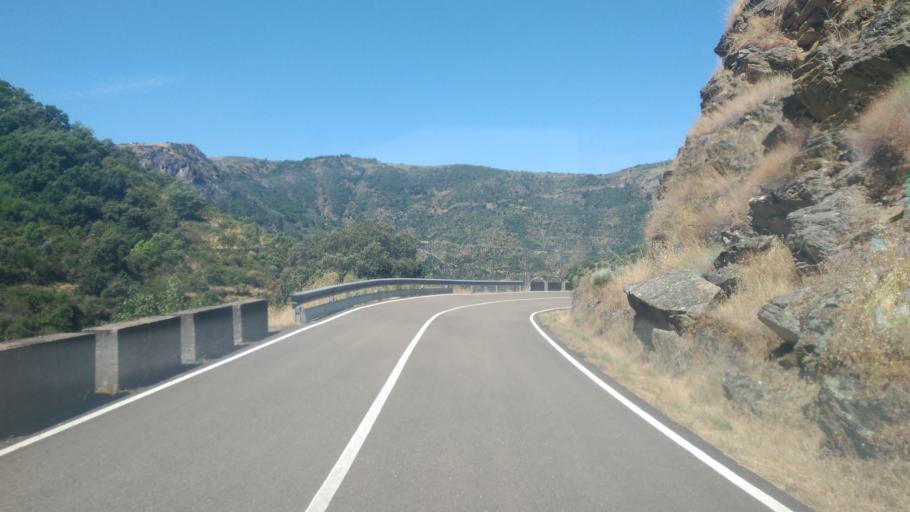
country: ES
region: Castille and Leon
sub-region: Provincia de Salamanca
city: Mieza
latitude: 41.1875
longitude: -6.6792
